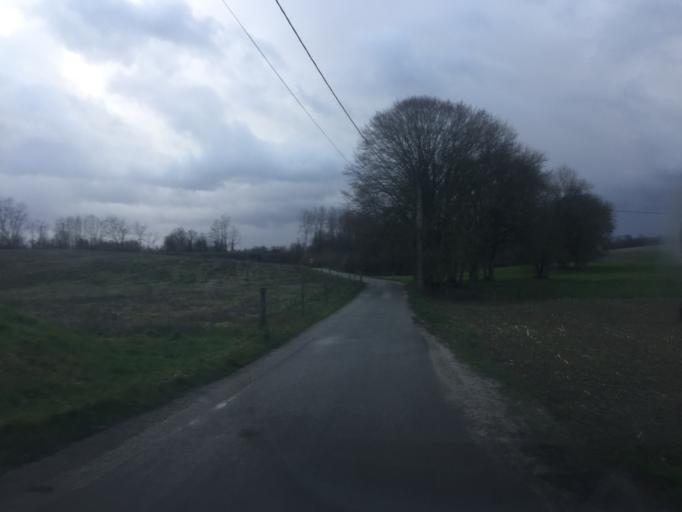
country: FR
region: Franche-Comte
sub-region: Departement du Jura
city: Fraisans
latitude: 47.1714
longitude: 5.7694
